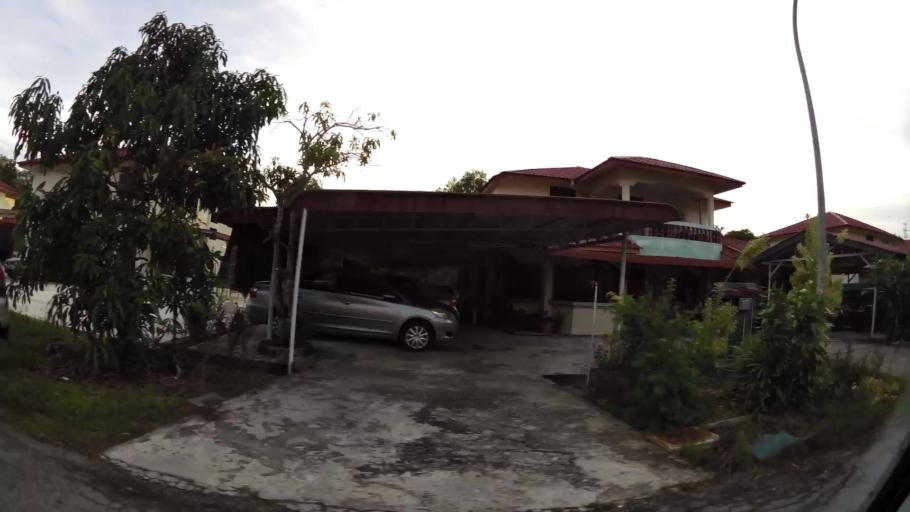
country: BN
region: Brunei and Muara
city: Bandar Seri Begawan
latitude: 4.9313
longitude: 114.8856
